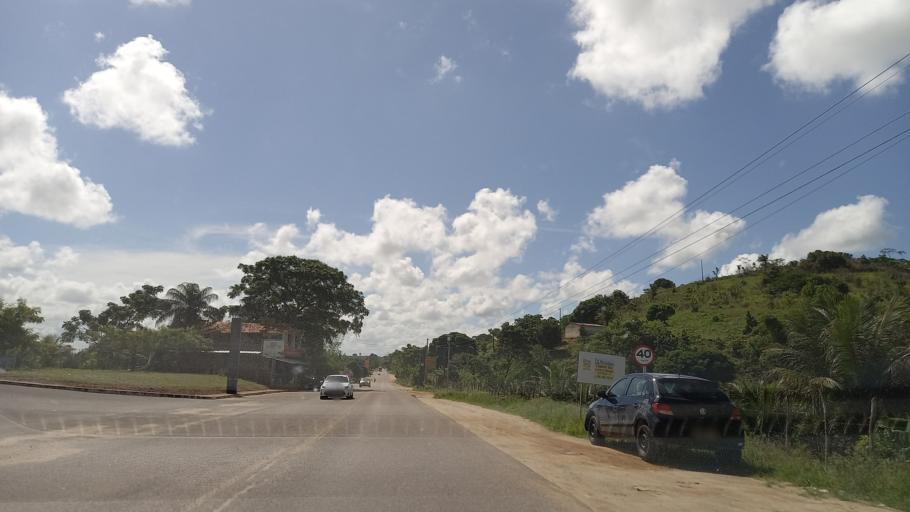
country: BR
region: Pernambuco
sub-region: Barreiros
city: Barreiros
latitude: -8.8064
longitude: -35.1857
